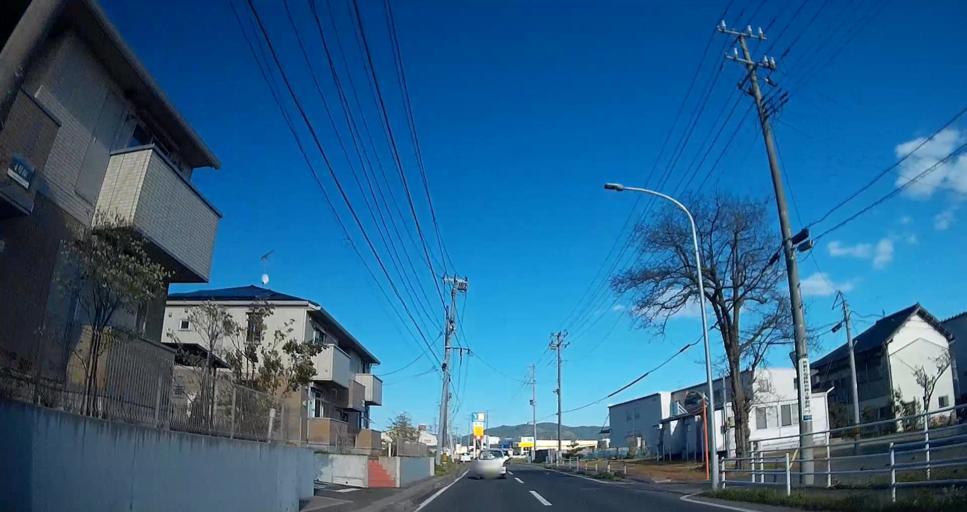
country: JP
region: Miyagi
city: Ishinomaki
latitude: 38.4200
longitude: 141.3298
